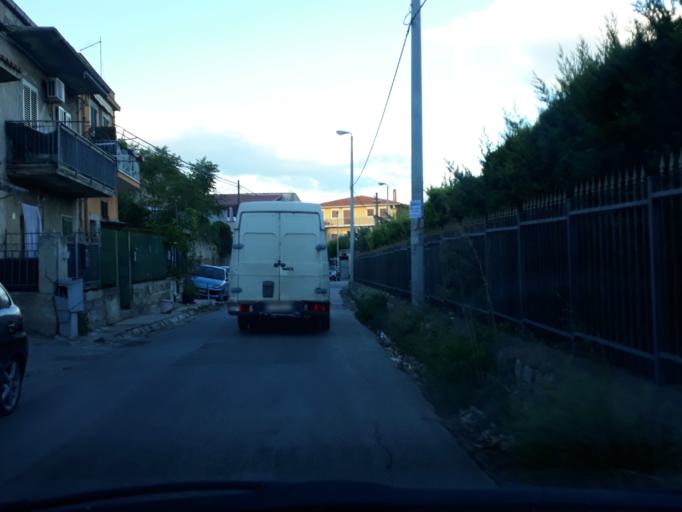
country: IT
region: Sicily
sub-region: Palermo
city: Villa Ciambra
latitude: 38.0781
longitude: 13.3126
